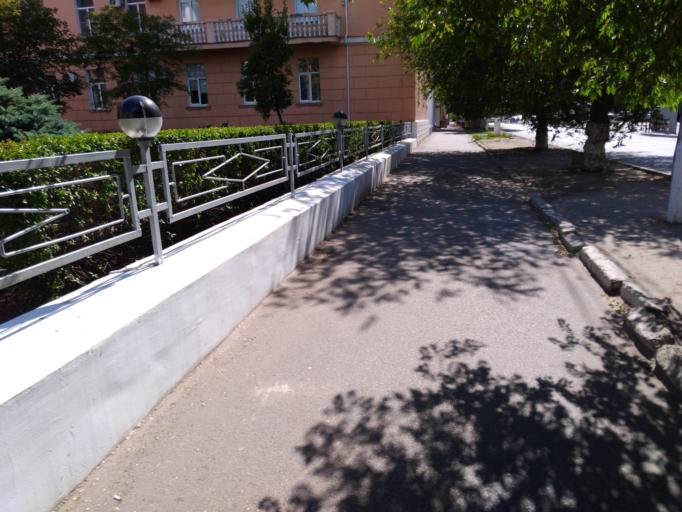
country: RU
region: Volgograd
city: Volgograd
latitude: 48.7160
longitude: 44.5241
